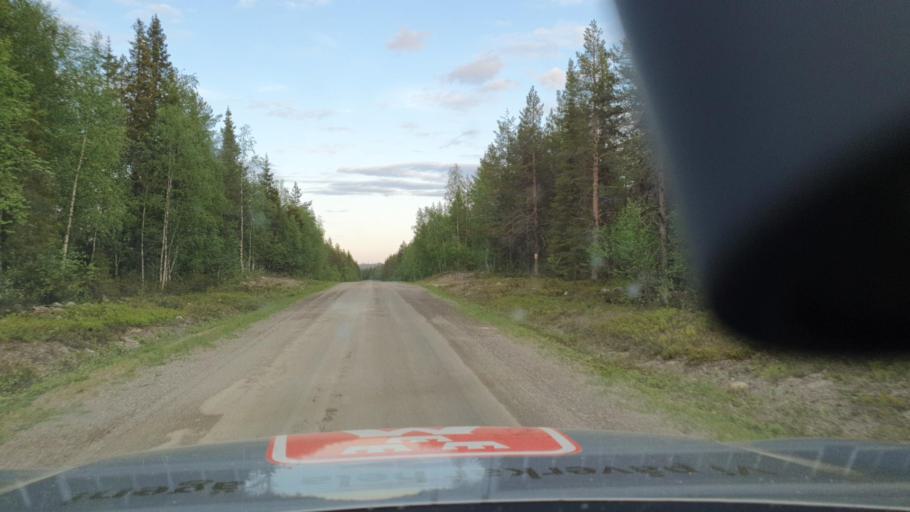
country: SE
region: Norrbotten
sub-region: Bodens Kommun
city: Boden
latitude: 66.5876
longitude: 21.3888
